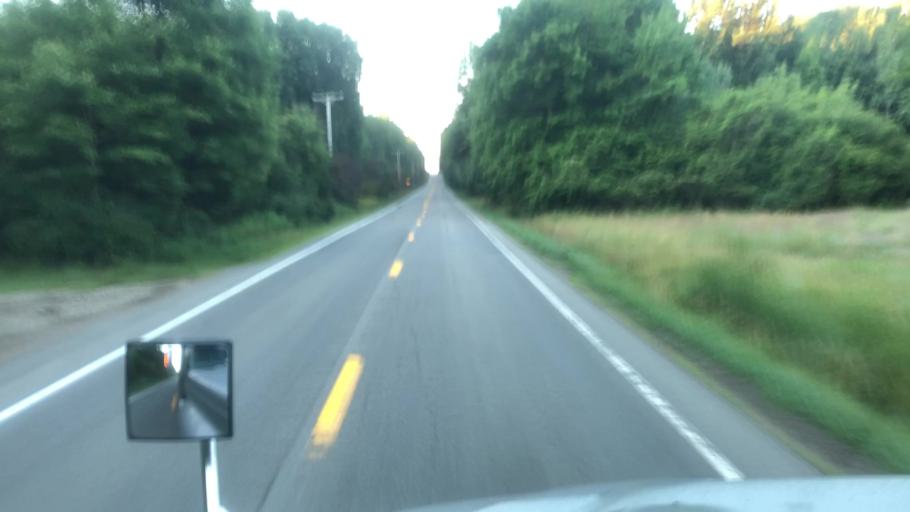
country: US
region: Pennsylvania
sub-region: Crawford County
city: Titusville
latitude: 41.5571
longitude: -79.6111
